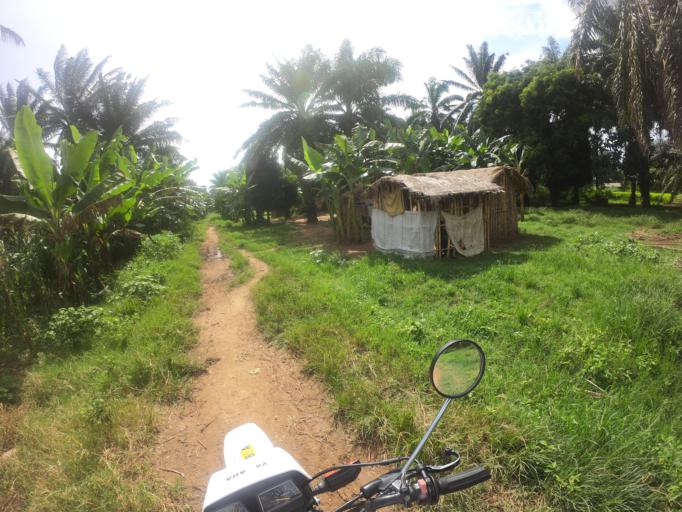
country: TZ
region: Mbeya
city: Kyela
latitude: -9.6531
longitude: 33.8246
